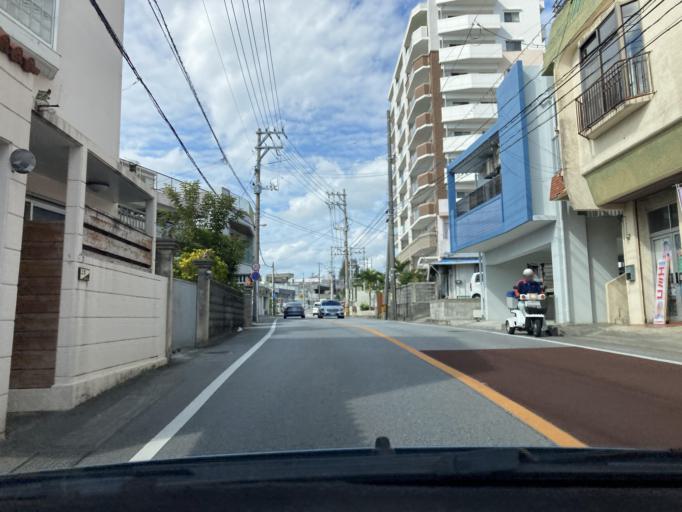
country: JP
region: Okinawa
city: Chatan
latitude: 26.3159
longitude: 127.7724
